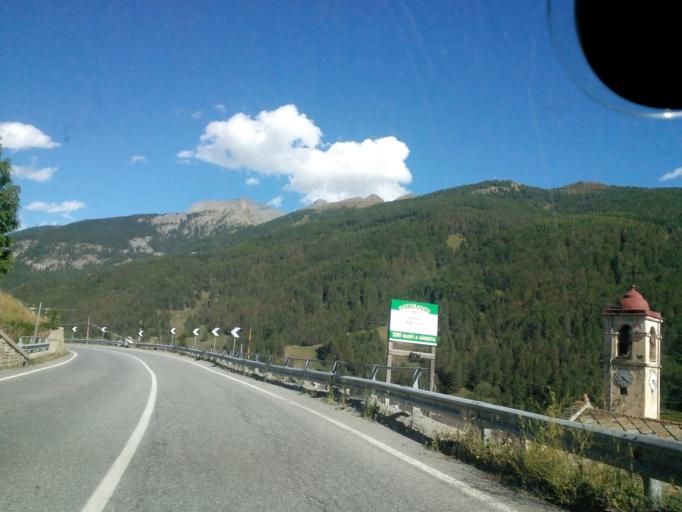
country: IT
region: Piedmont
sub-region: Provincia di Torino
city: Pragelato-Rua
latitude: 44.9969
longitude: 6.9200
